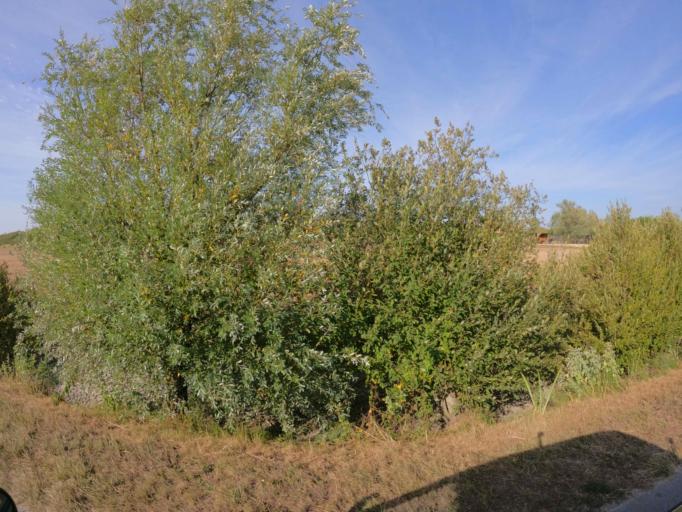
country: FR
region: Pays de la Loire
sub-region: Departement de la Vendee
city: Le Perrier
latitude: 46.8085
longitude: -1.9875
